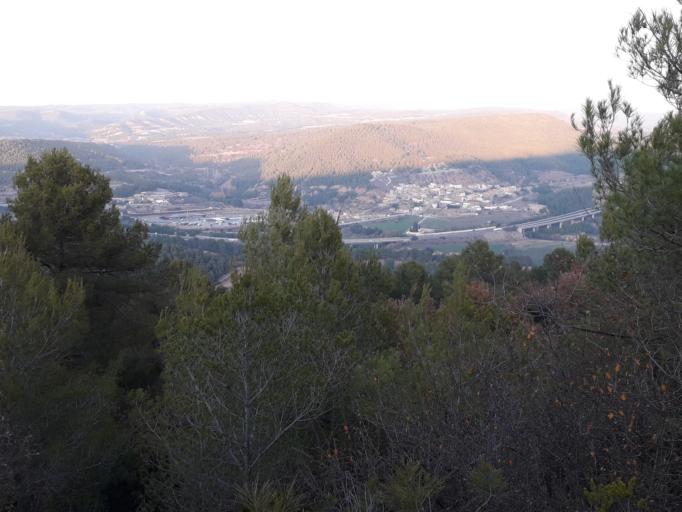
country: ES
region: Catalonia
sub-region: Provincia de Barcelona
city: Jorba
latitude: 41.5923
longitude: 1.5325
